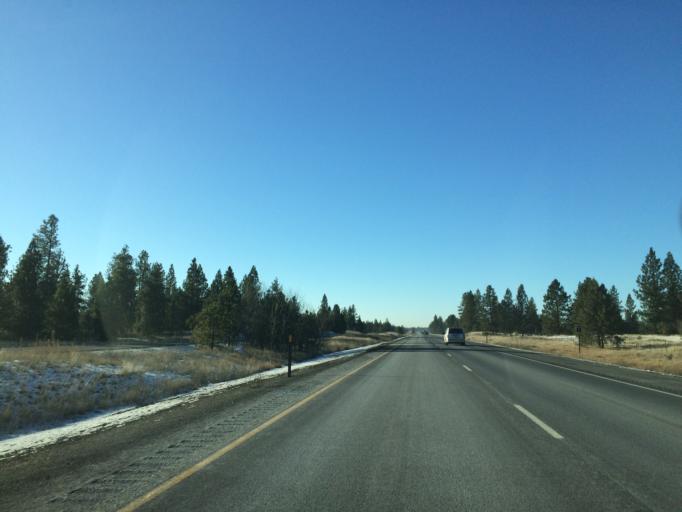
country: US
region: Washington
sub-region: Spokane County
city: Medical Lake
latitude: 47.4559
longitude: -117.7623
